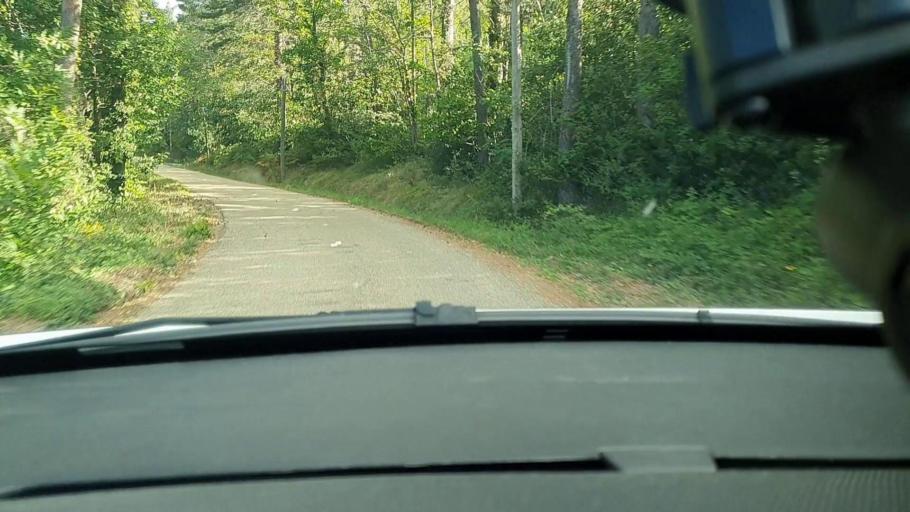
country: FR
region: Languedoc-Roussillon
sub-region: Departement du Gard
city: Besseges
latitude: 44.3852
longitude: 3.9911
